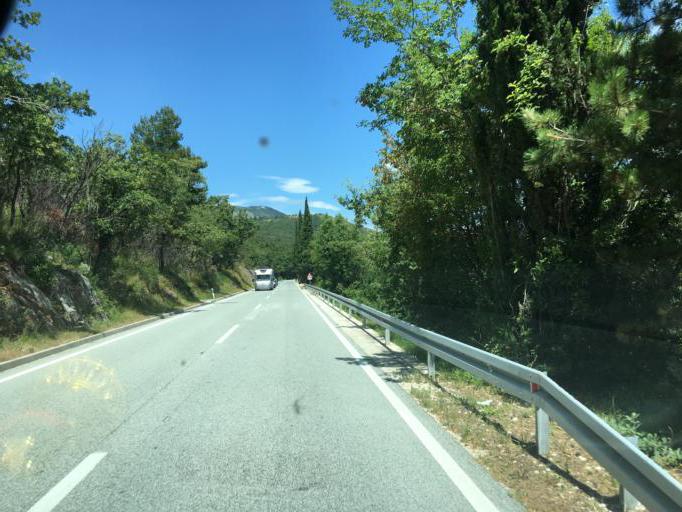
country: HR
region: Istarska
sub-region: Grad Labin
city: Rabac
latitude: 45.1287
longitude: 14.2045
